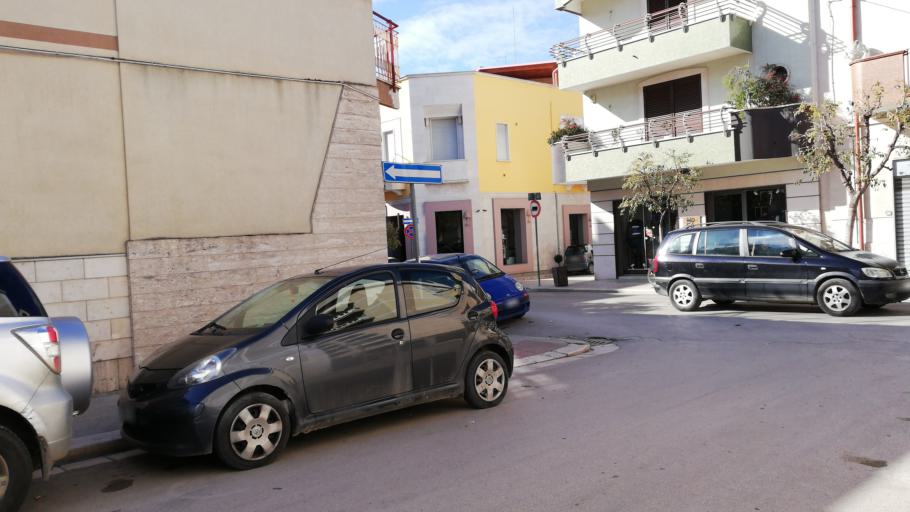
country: IT
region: Apulia
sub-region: Provincia di Barletta - Andria - Trani
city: Andria
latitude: 41.2209
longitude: 16.3025
